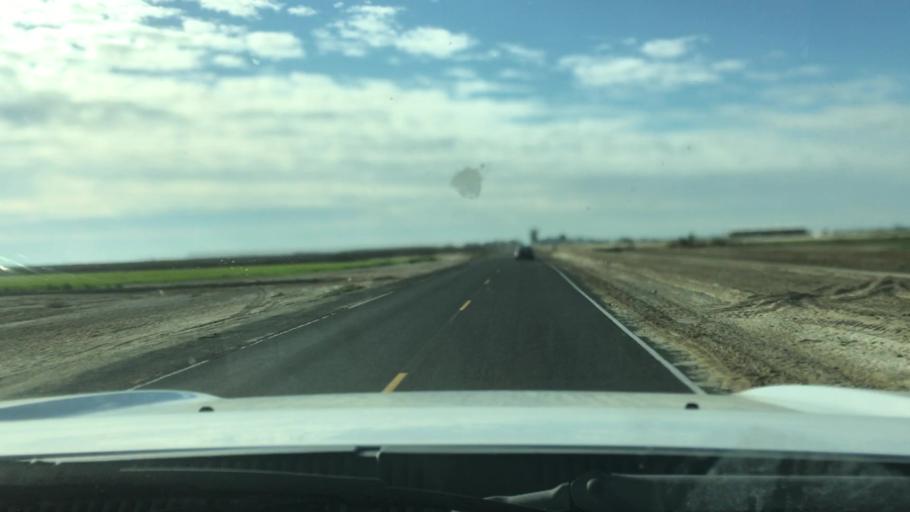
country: US
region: California
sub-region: Kings County
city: Stratford
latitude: 36.2201
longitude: -119.7624
